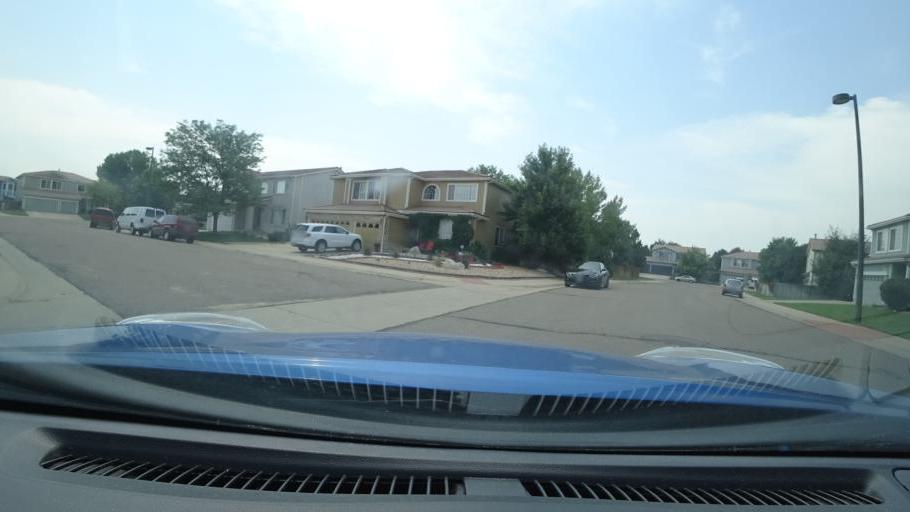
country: US
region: Colorado
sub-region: Adams County
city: Aurora
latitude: 39.7744
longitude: -104.7670
